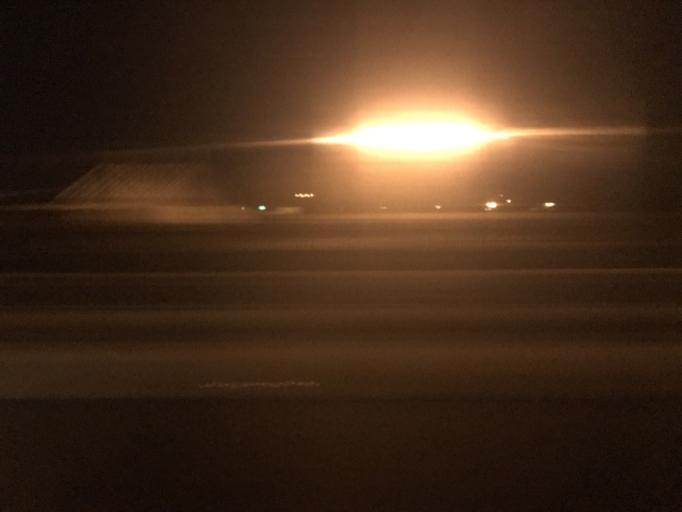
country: US
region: Texas
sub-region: Jones County
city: Anson
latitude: 32.7331
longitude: -99.8945
